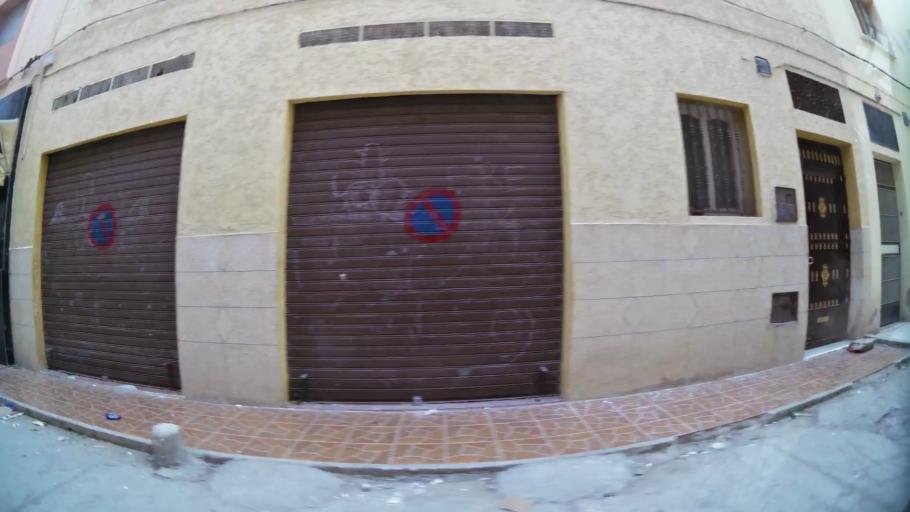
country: MA
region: Oriental
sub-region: Nador
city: Nador
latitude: 35.1713
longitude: -2.9268
